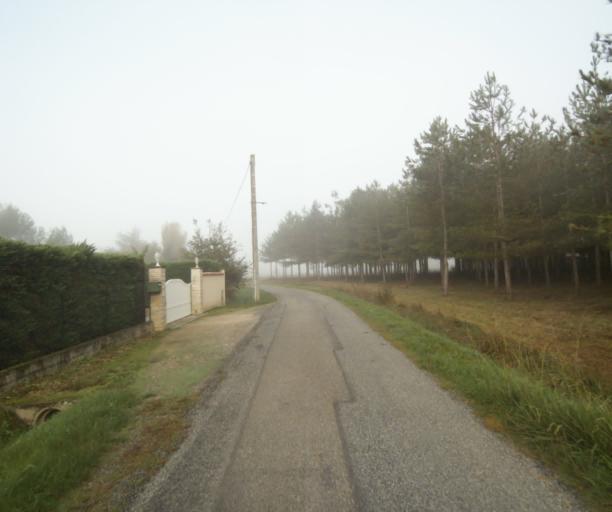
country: FR
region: Midi-Pyrenees
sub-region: Departement du Tarn-et-Garonne
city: Nohic
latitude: 43.8957
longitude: 1.4465
